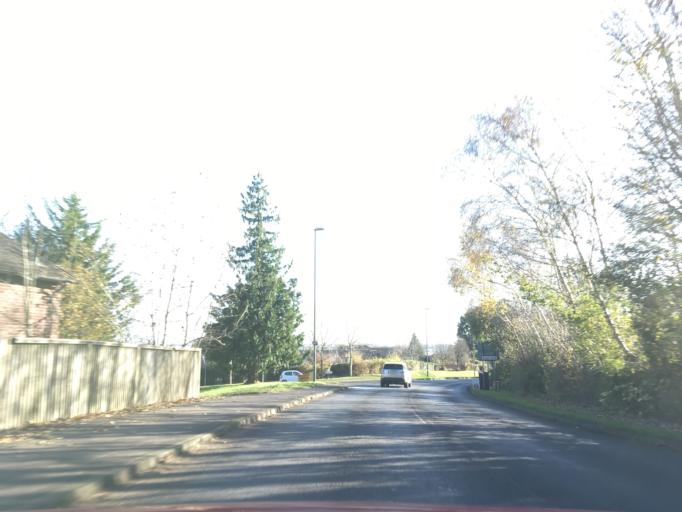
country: GB
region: England
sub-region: Hampshire
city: Compton
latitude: 51.0495
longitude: -1.3454
